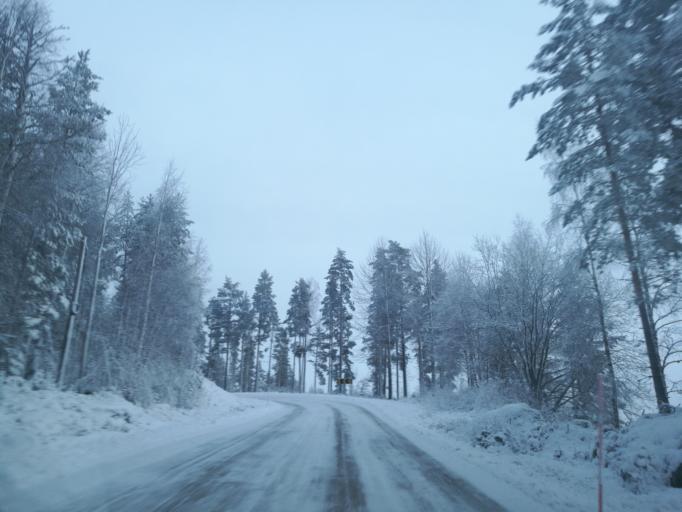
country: NO
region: Hedmark
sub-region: Grue
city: Kirkenaer
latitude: 60.4375
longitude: 12.4575
